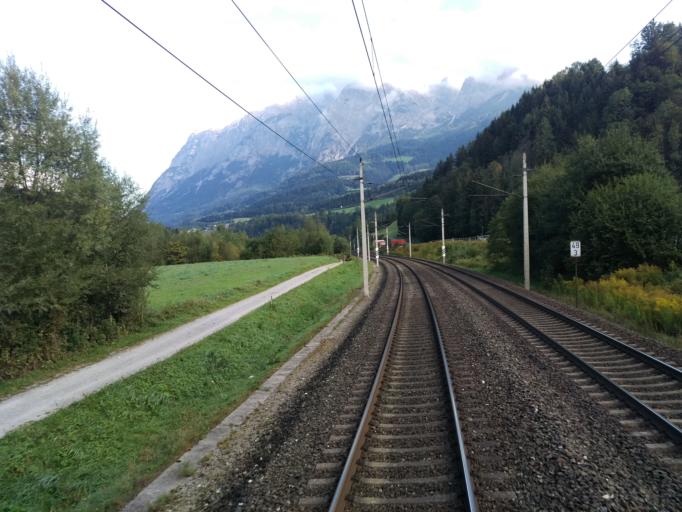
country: AT
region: Salzburg
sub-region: Politischer Bezirk Sankt Johann im Pongau
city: Pfarrwerfen
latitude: 47.4413
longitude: 13.2131
